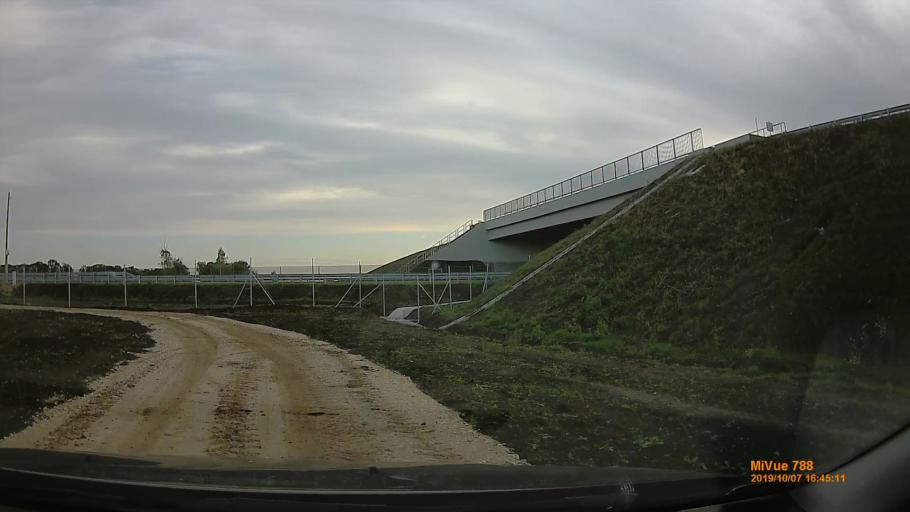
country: HU
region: Bekes
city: Szarvas
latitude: 46.8191
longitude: 20.6051
